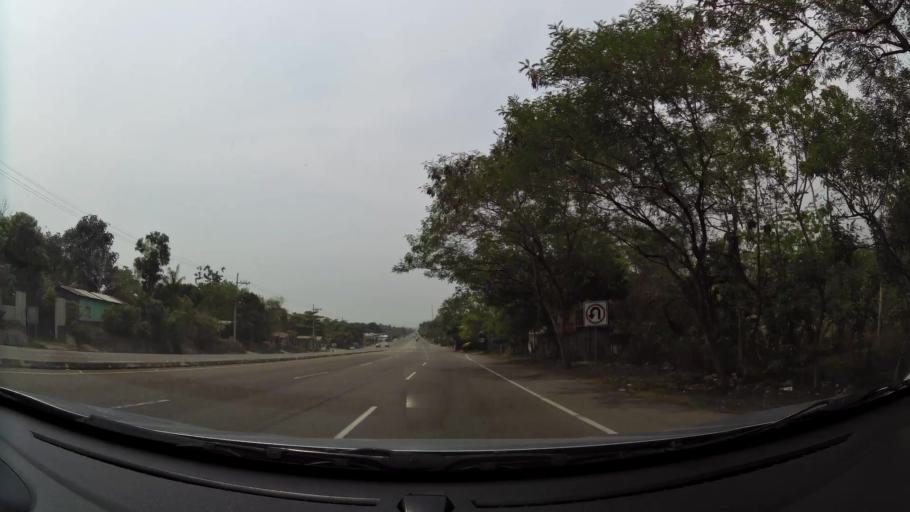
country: HN
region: Cortes
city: Oropendolas
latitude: 15.0332
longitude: -87.9279
